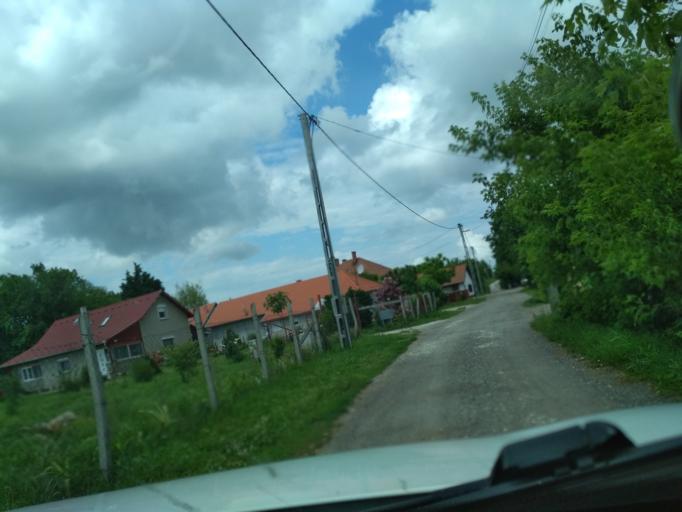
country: HU
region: Jasz-Nagykun-Szolnok
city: Tiszafured
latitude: 47.6060
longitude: 20.7476
